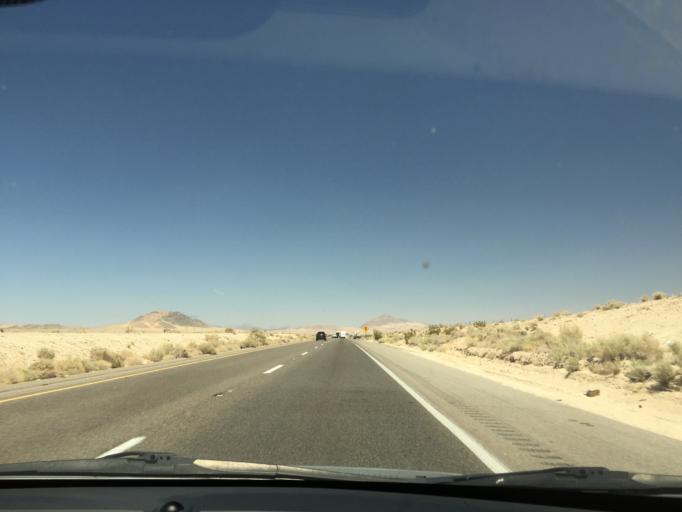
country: US
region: California
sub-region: San Bernardino County
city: Fort Irwin
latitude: 35.0110
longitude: -116.5308
